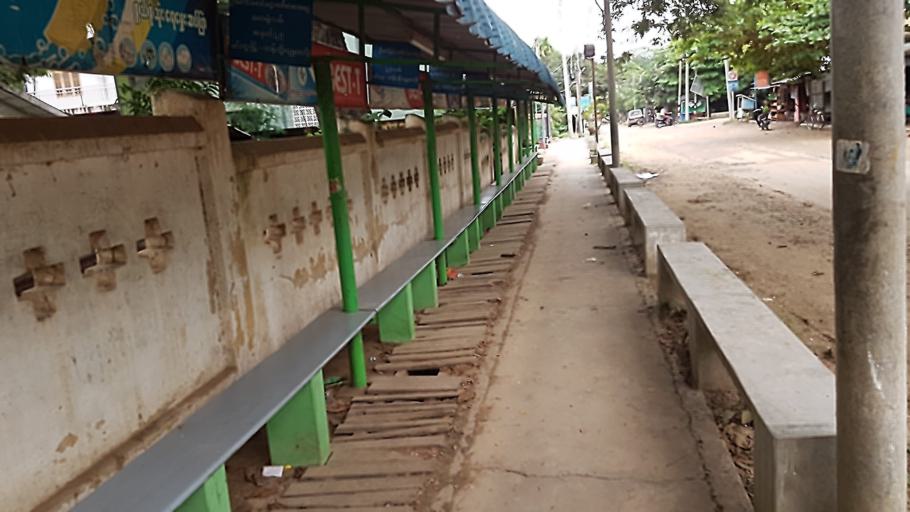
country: MM
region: Magway
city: Minbu
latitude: 20.1738
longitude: 94.8771
